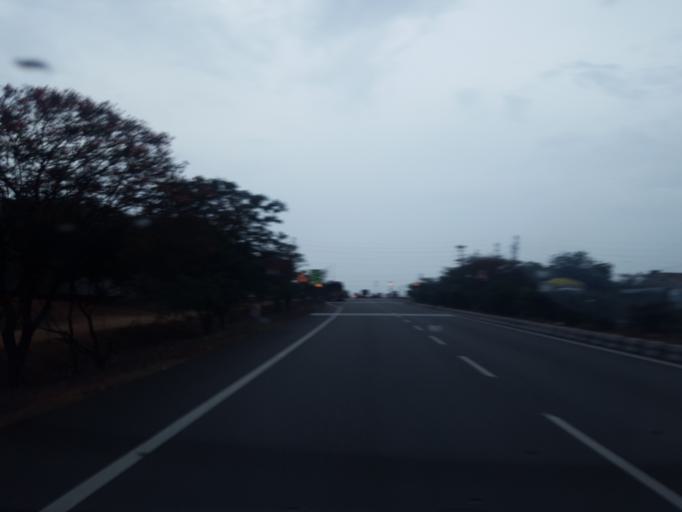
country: IN
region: Telangana
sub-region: Mahbubnagar
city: Farrukhnagar
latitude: 17.1382
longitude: 78.2868
